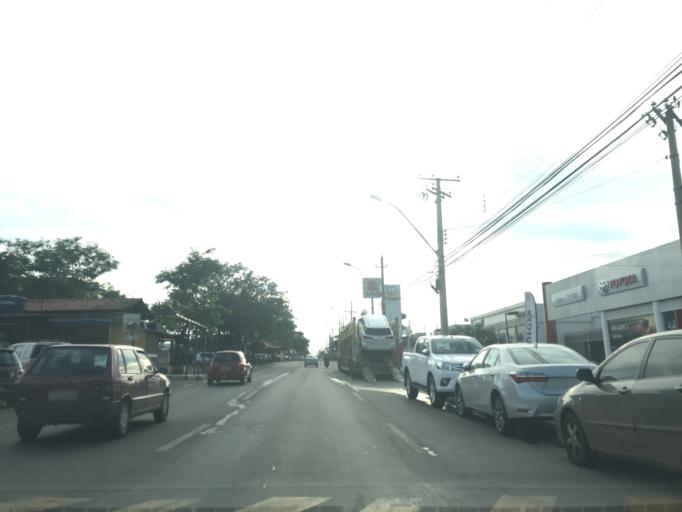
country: BR
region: Federal District
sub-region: Brasilia
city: Brasilia
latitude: -15.8057
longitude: -47.9633
